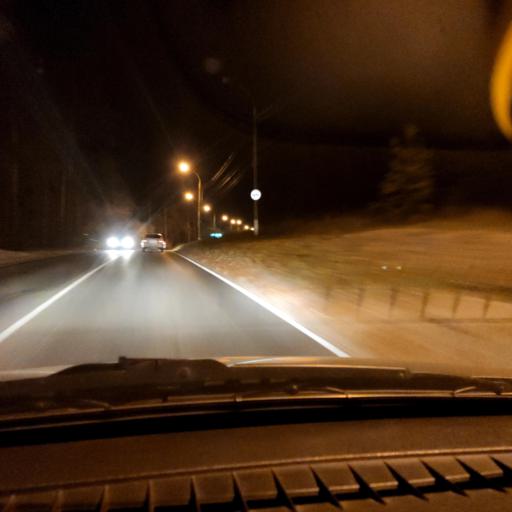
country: RU
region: Samara
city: Tol'yatti
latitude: 53.4825
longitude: 49.3197
